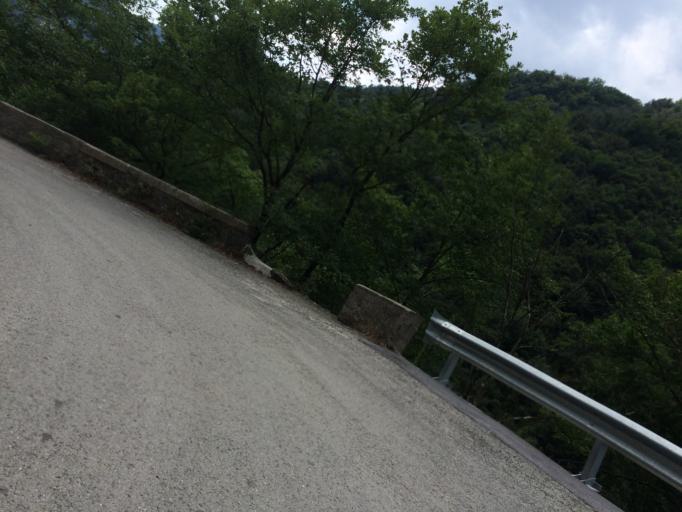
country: IT
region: Liguria
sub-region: Provincia di Imperia
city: Castel Vittorio
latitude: 43.9432
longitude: 7.6859
